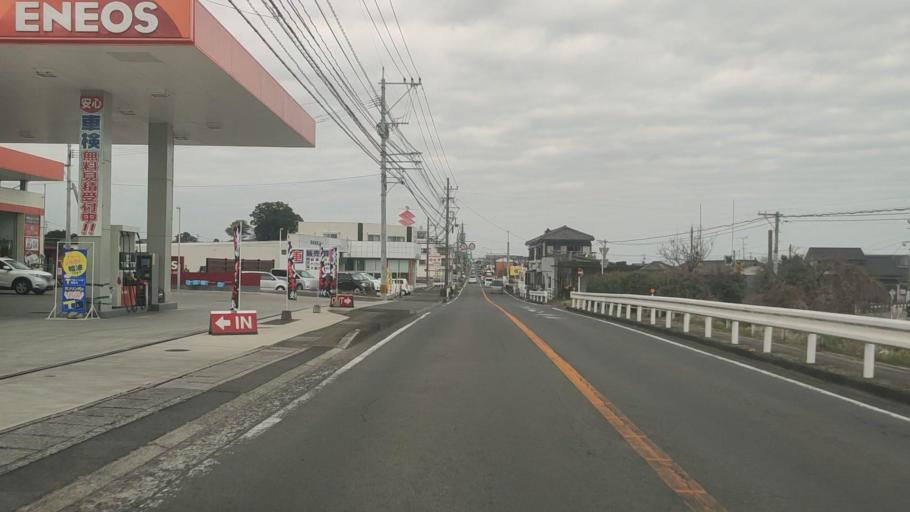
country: JP
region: Nagasaki
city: Shimabara
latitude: 32.8226
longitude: 130.3532
